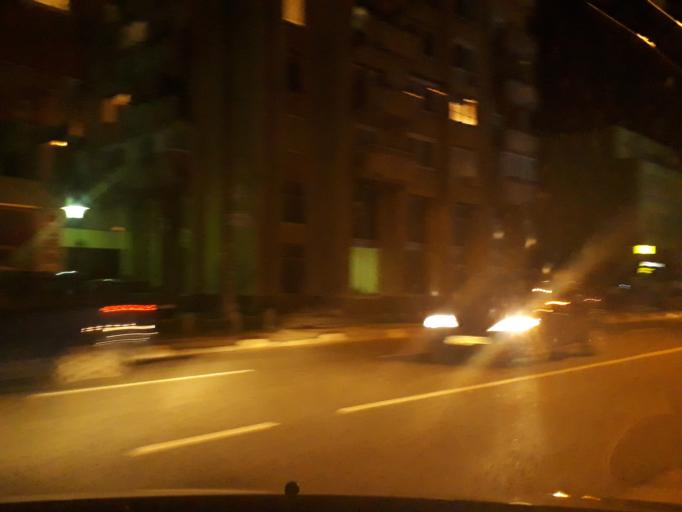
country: BA
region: Federation of Bosnia and Herzegovina
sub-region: Kanton Sarajevo
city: Sarajevo
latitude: 43.8475
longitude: 18.3757
